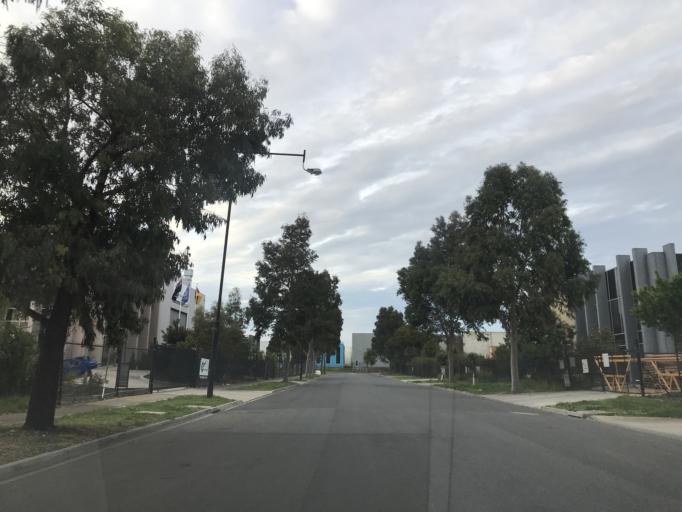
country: AU
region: Victoria
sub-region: Wyndham
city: Truganina
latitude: -37.8014
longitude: 144.7558
